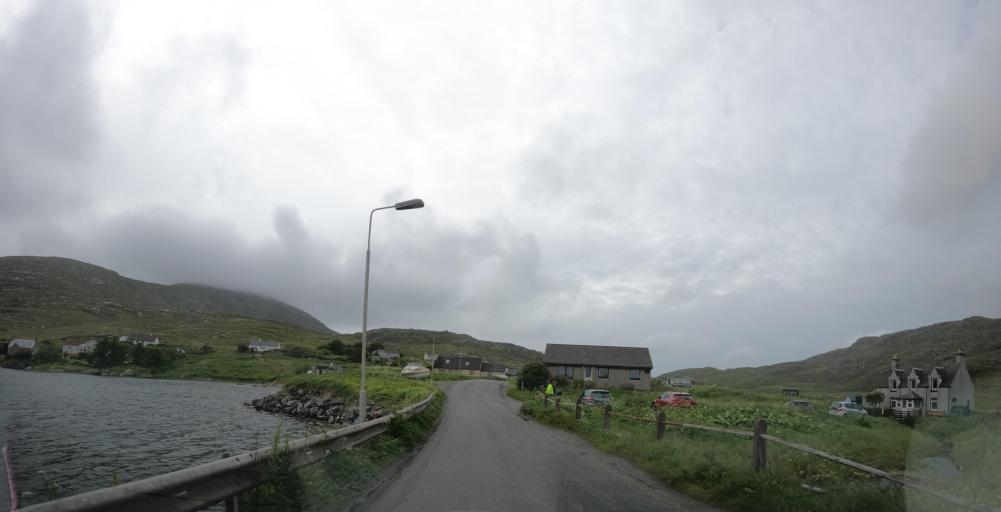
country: GB
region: Scotland
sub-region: Eilean Siar
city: Barra
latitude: 56.9576
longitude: -7.5027
